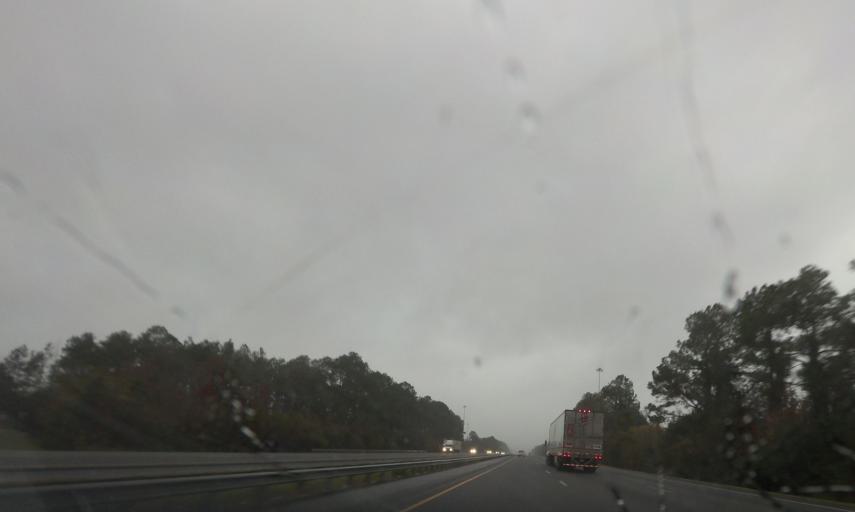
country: US
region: Georgia
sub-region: Lowndes County
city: Valdosta
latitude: 30.7785
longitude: -83.2960
